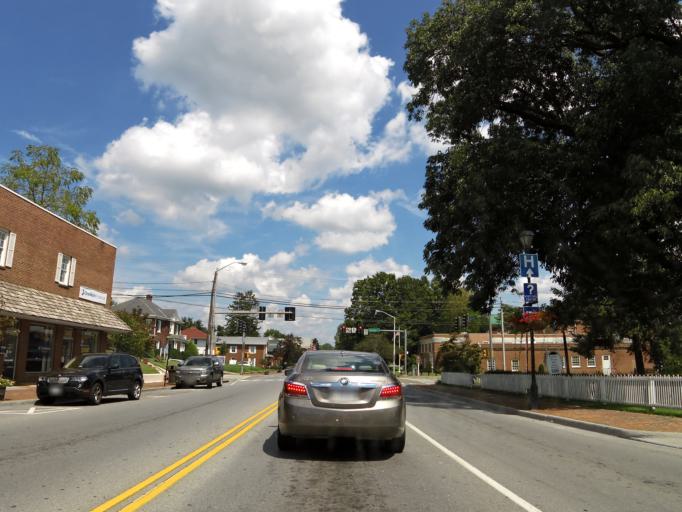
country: US
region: Virginia
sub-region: Washington County
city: Abingdon
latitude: 36.7096
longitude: -81.9779
